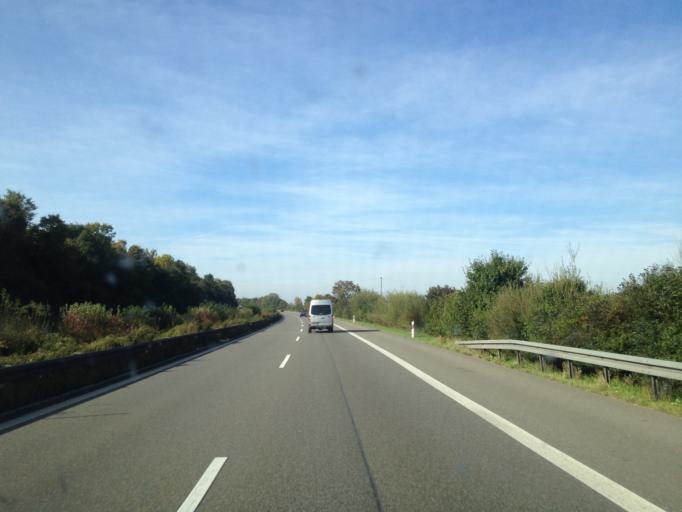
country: DE
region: Baden-Wuerttemberg
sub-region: Regierungsbezirk Stuttgart
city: Bondorf
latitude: 48.4830
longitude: 8.8075
